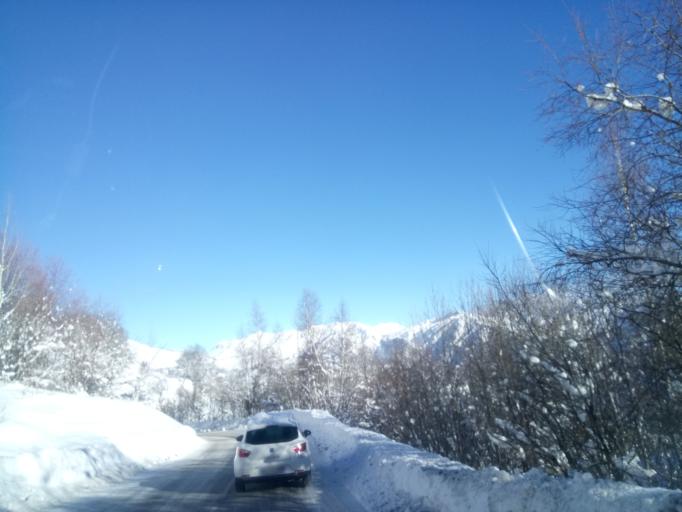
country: FR
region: Rhone-Alpes
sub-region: Departement de la Savoie
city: Saint-Jean-de-Maurienne
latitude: 45.2356
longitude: 6.2770
